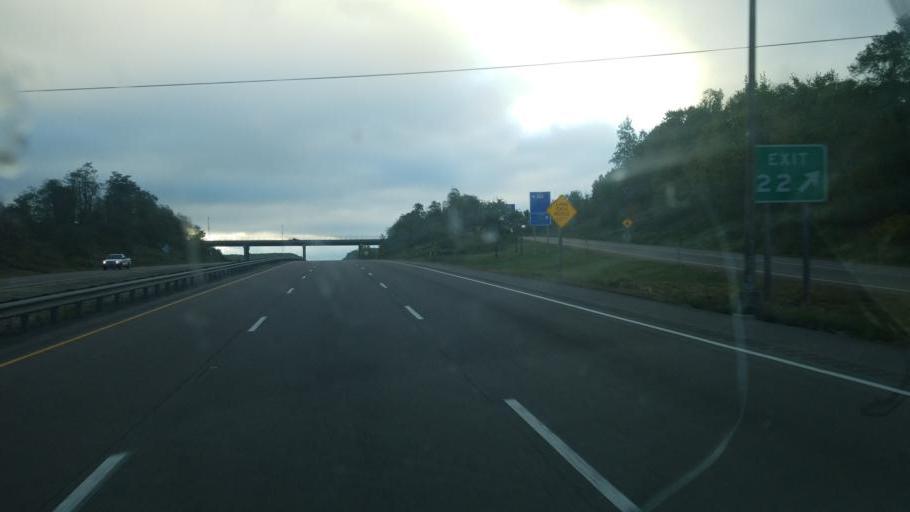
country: US
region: Pennsylvania
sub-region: Somerset County
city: Meyersdale
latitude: 39.6900
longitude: -79.1088
